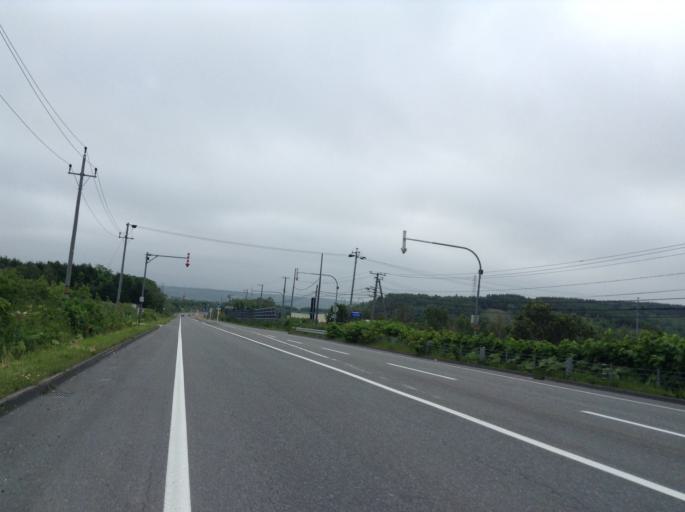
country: JP
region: Hokkaido
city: Wakkanai
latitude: 45.3715
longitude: 141.7212
